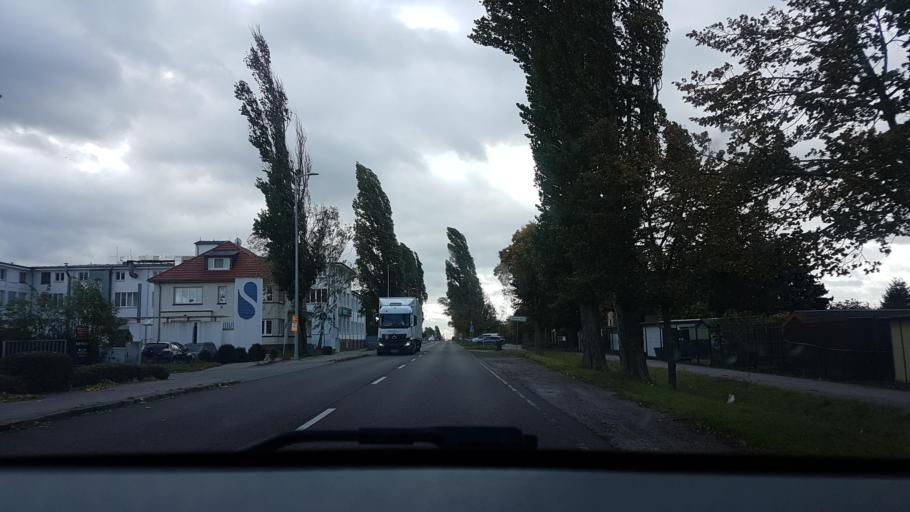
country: DE
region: Saxony-Anhalt
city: Bernburg
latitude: 51.7820
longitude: 11.7451
